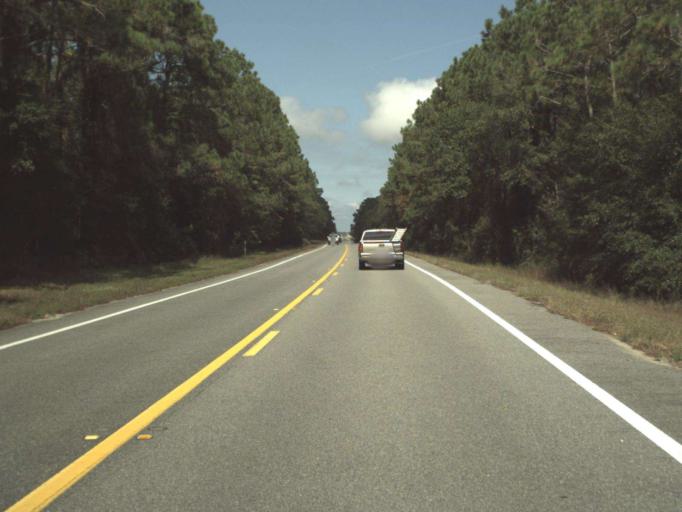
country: US
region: Florida
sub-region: Wakulla County
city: Crawfordville
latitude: 29.9466
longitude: -84.3860
